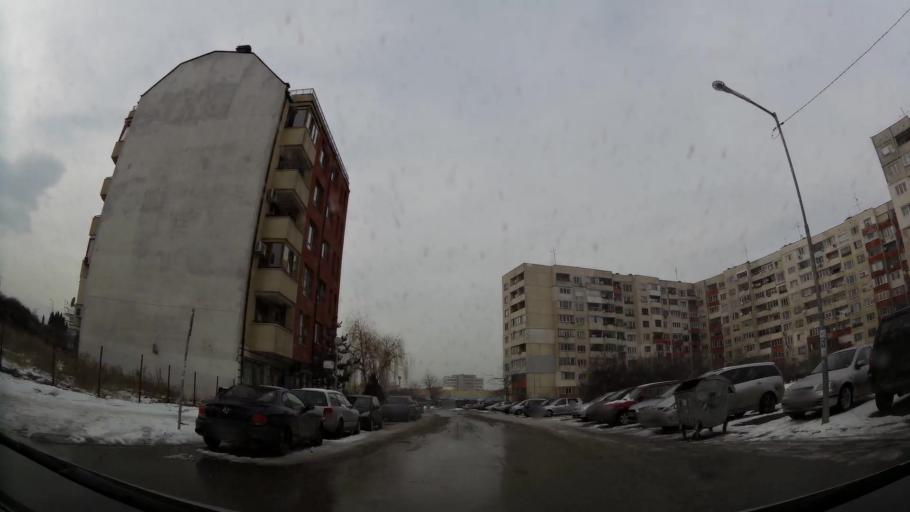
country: BG
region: Sofia-Capital
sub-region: Stolichna Obshtina
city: Sofia
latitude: 42.7108
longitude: 23.3771
